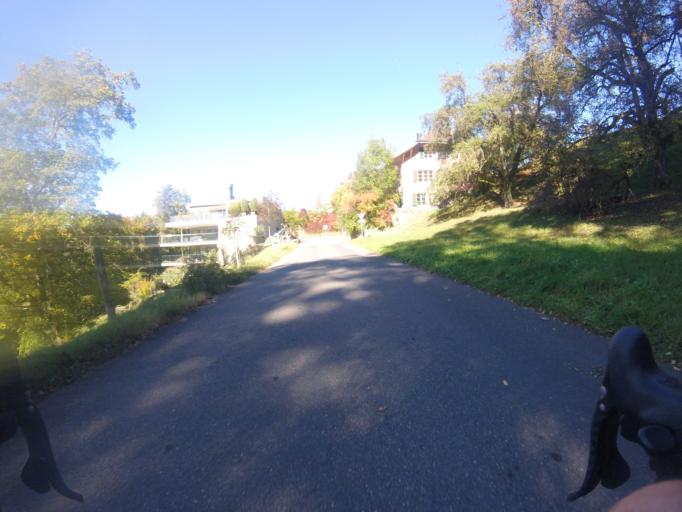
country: CH
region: Bern
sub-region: Bern-Mittelland District
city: Wohlen
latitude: 46.9702
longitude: 7.3515
